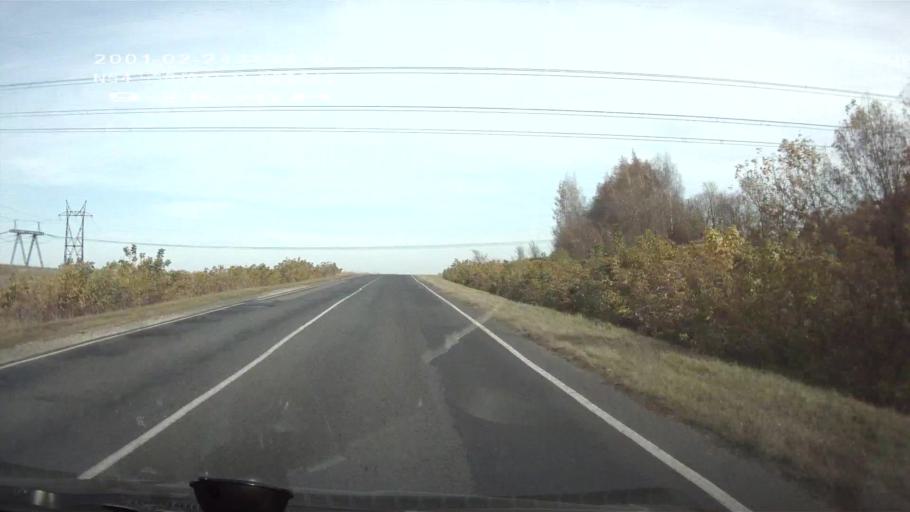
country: RU
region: Mordoviya
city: Atyashevo
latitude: 54.5367
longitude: 45.9250
